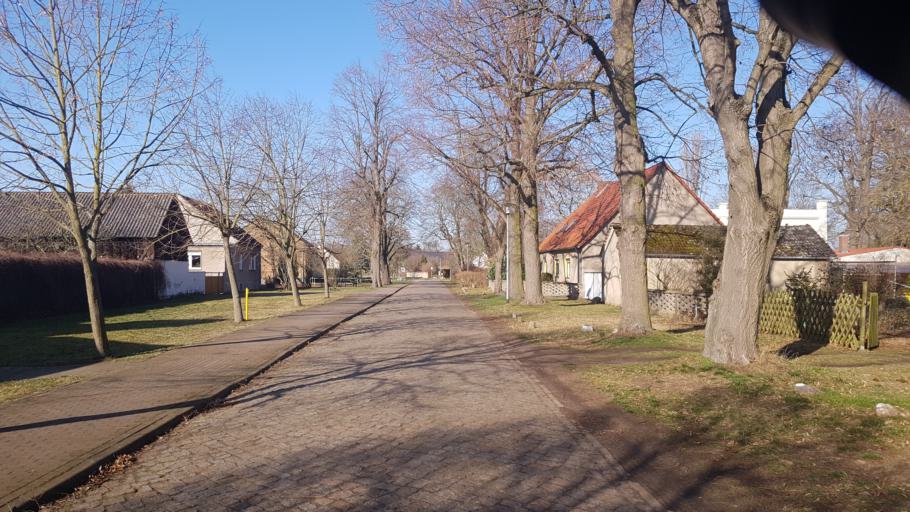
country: DE
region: Brandenburg
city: Luckau
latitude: 51.8347
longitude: 13.7992
